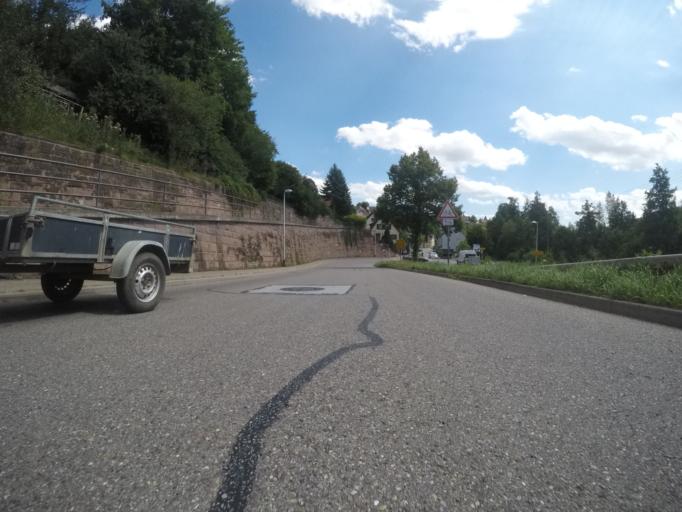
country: DE
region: Baden-Wuerttemberg
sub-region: Karlsruhe Region
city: Ebhausen
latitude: 48.5891
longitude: 8.6730
